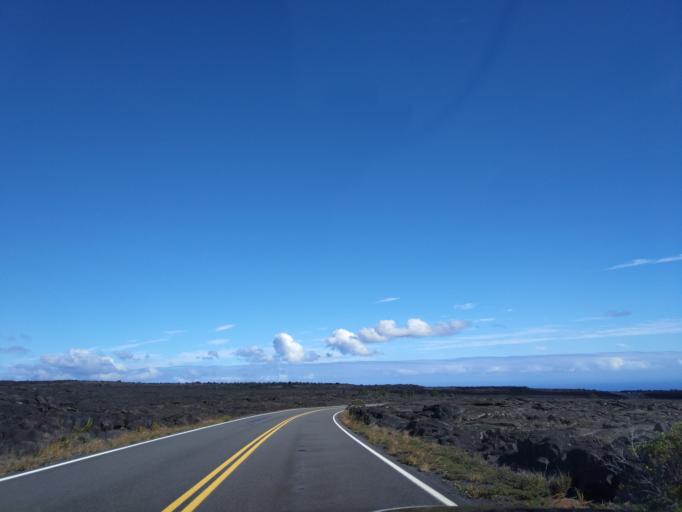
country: US
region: Hawaii
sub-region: Hawaii County
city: Volcano
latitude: 19.3317
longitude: -155.1972
